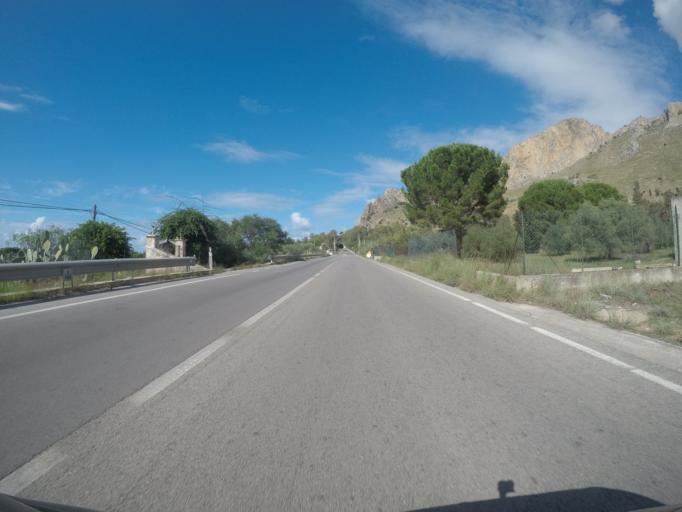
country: IT
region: Sicily
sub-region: Palermo
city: Agliandroni-Paternella
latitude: 38.1201
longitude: 13.0760
